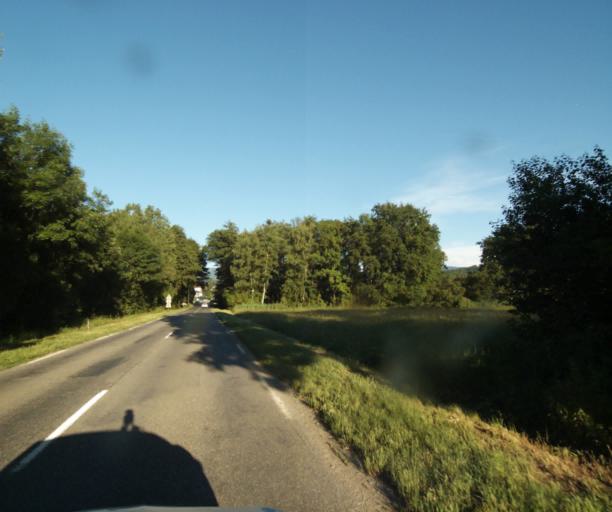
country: FR
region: Rhone-Alpes
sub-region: Departement de la Haute-Savoie
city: Sciez
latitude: 46.3346
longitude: 6.3667
